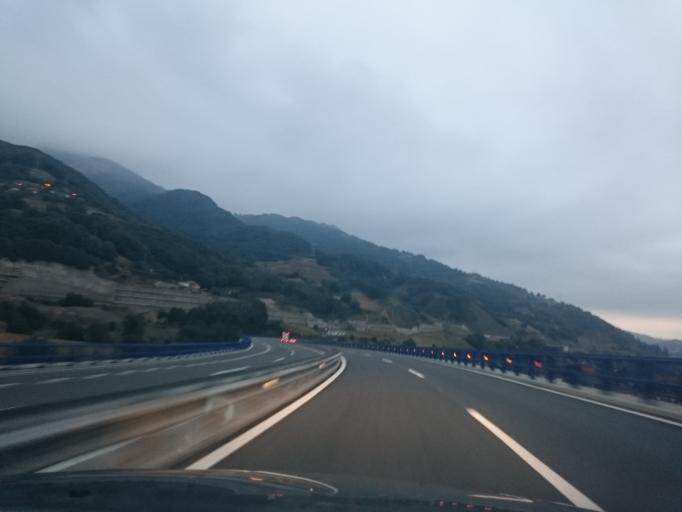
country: ES
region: Asturias
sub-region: Province of Asturias
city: Pola de Lena
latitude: 43.1027
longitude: -5.8189
